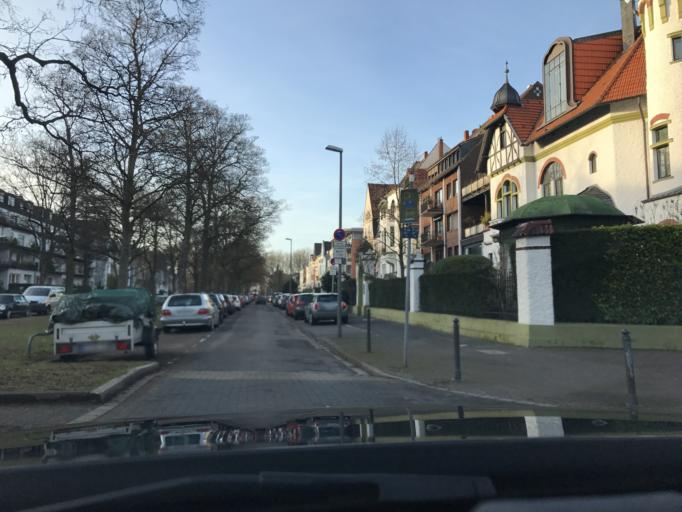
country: DE
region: North Rhine-Westphalia
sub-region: Regierungsbezirk Dusseldorf
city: Krefeld
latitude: 51.3406
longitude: 6.5742
